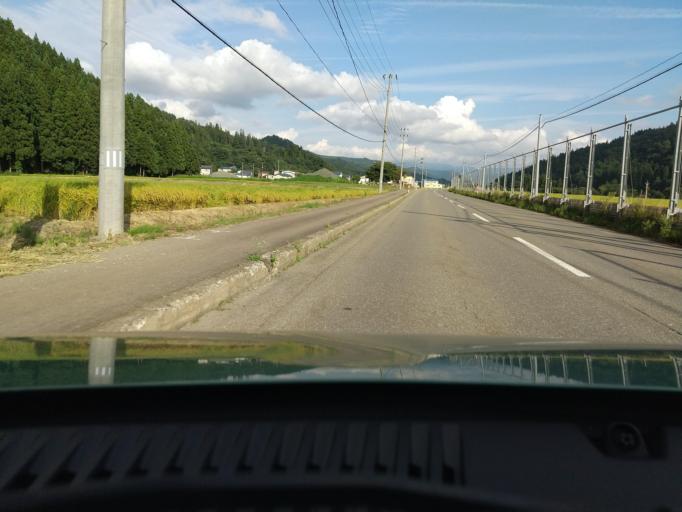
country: JP
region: Akita
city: Yuzawa
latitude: 39.2012
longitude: 140.5849
